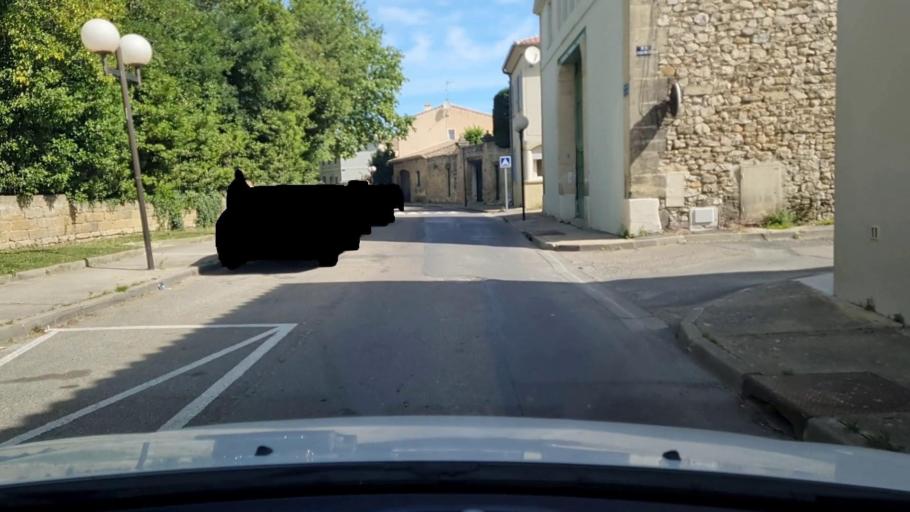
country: FR
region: Languedoc-Roussillon
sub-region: Departement de l'Herault
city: Marsillargues
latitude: 43.6358
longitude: 4.1959
